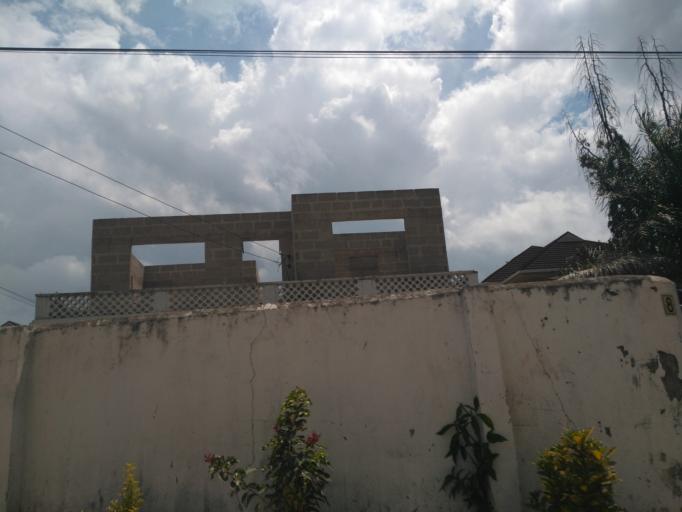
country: TZ
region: Dar es Salaam
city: Magomeni
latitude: -6.7557
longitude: 39.2417
